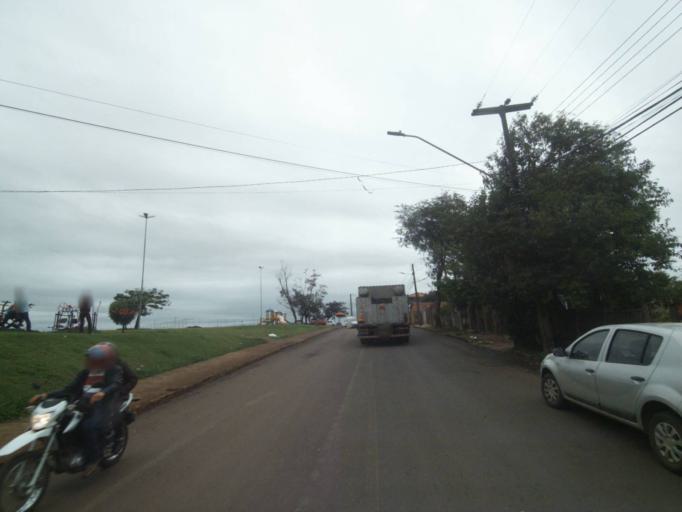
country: BR
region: Parana
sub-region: Telemaco Borba
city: Telemaco Borba
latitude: -24.3237
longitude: -50.6546
